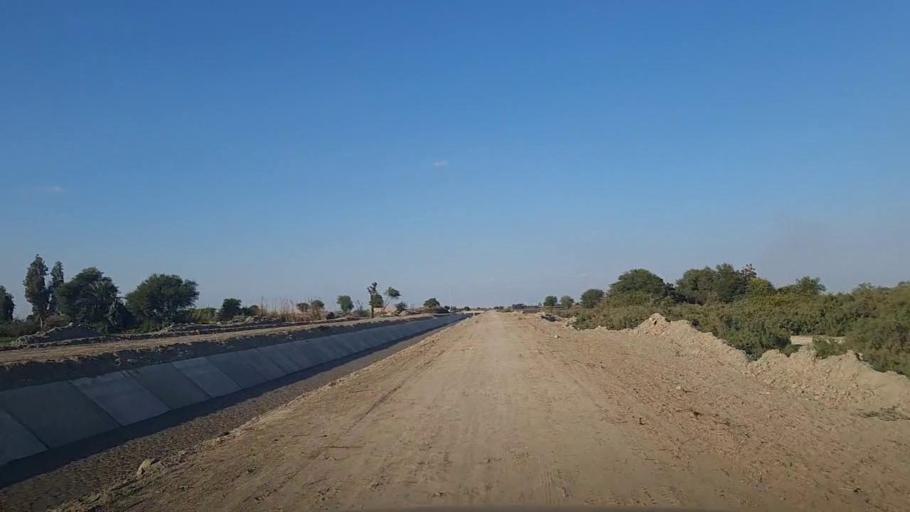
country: PK
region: Sindh
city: Jhol
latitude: 25.9166
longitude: 69.0408
